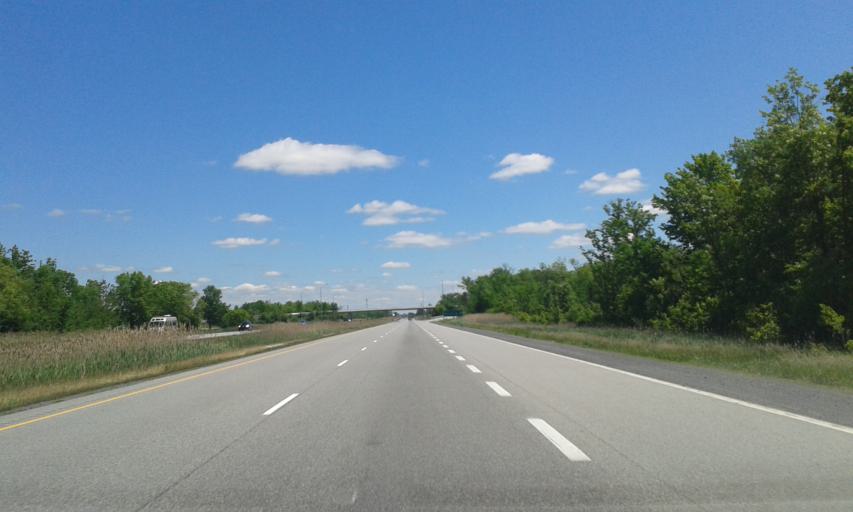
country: US
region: New York
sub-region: St. Lawrence County
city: Norfolk
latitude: 44.9508
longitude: -75.1157
